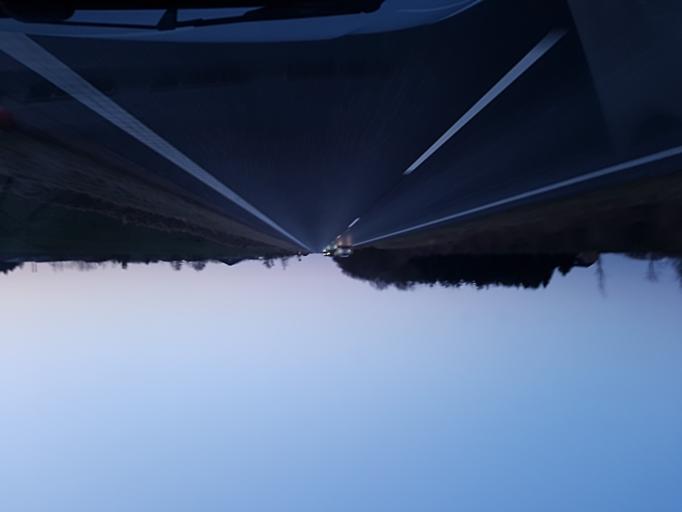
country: DK
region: Central Jutland
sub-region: Ringkobing-Skjern Kommune
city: Videbaek
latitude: 56.2053
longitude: 8.5812
